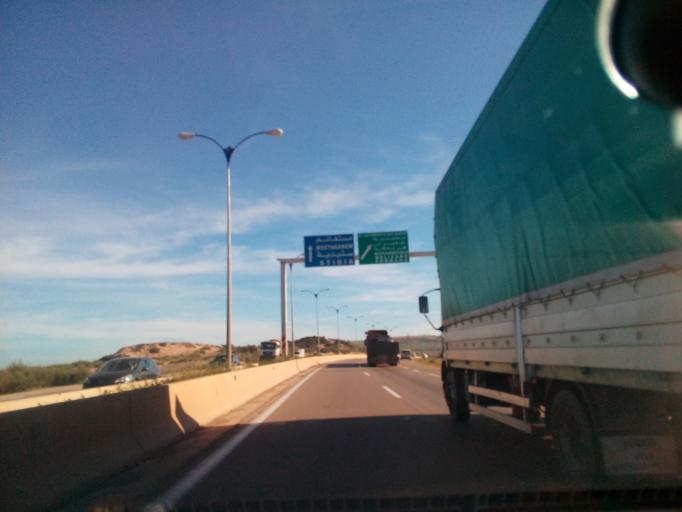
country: DZ
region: Oran
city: Ain el Bya
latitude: 35.7869
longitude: -0.1131
